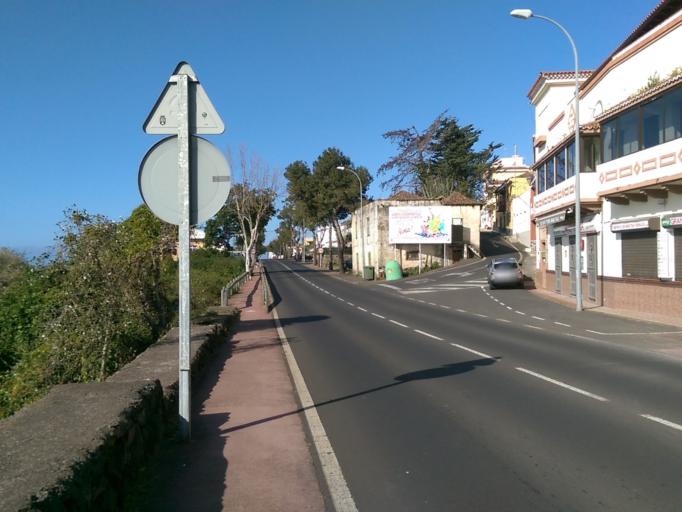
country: ES
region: Canary Islands
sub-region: Provincia de Santa Cruz de Tenerife
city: La Matanza de Acentejo
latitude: 28.4492
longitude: -16.4577
